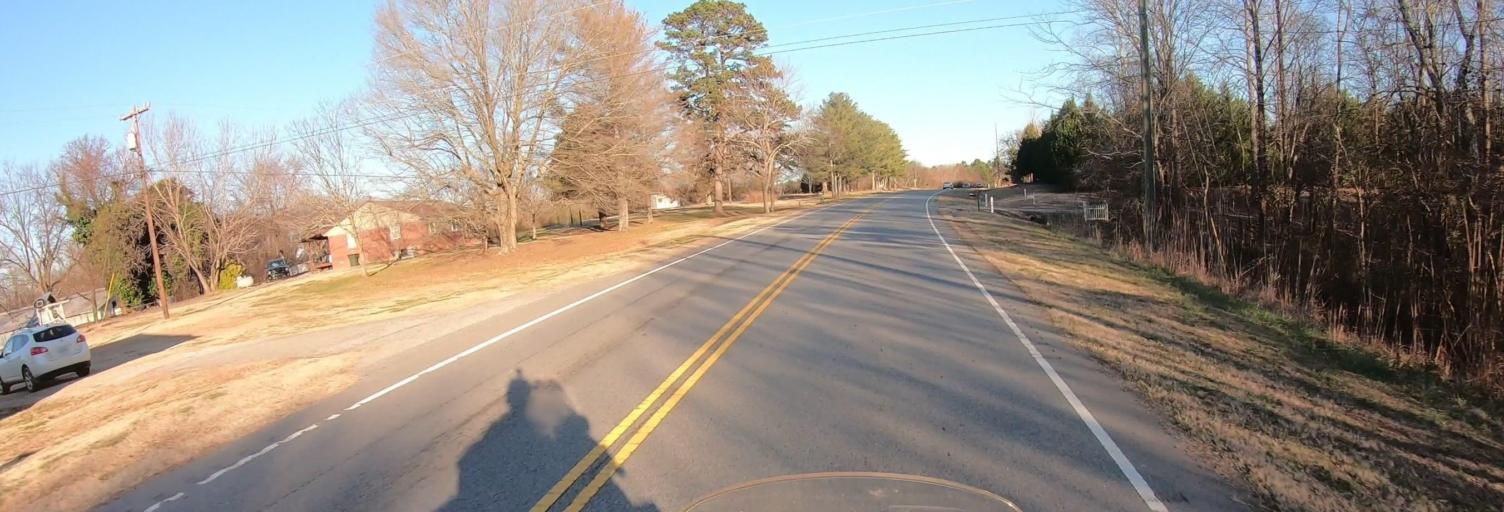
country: US
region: South Carolina
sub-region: Cherokee County
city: Gaffney
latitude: 35.1306
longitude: -81.7449
